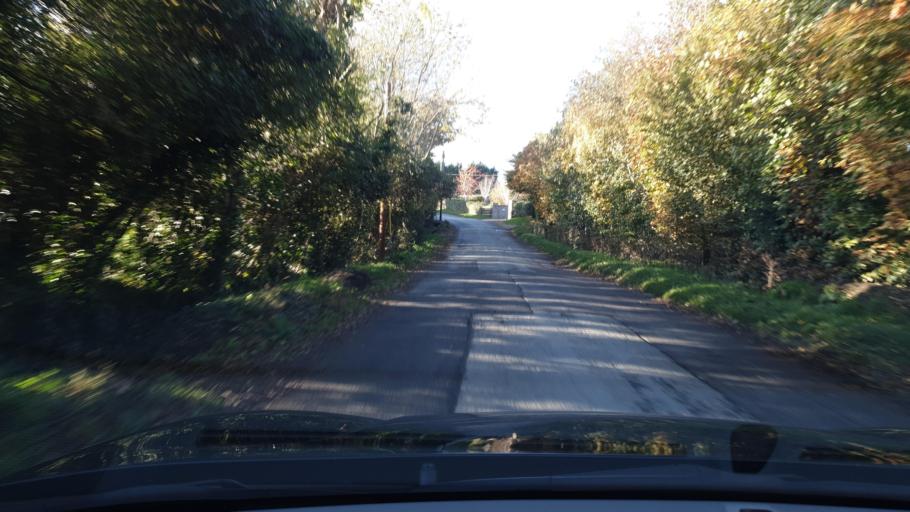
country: IE
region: Leinster
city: Balrothery
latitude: 53.5897
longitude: -6.1973
